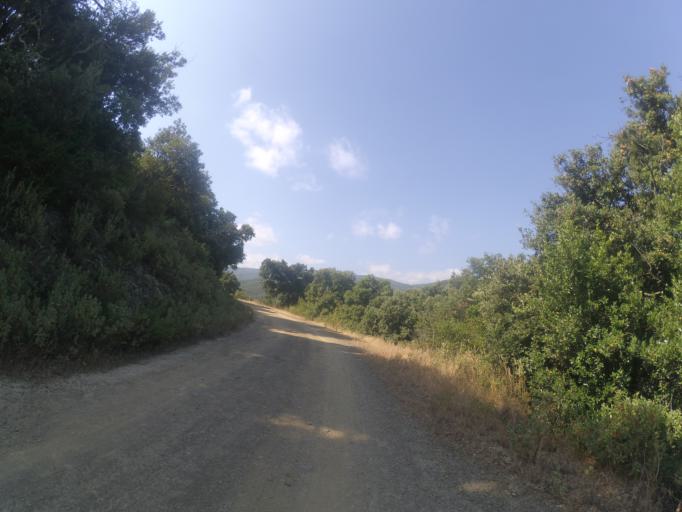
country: FR
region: Languedoc-Roussillon
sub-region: Departement des Pyrenees-Orientales
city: Ille-sur-Tet
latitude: 42.6510
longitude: 2.6255
